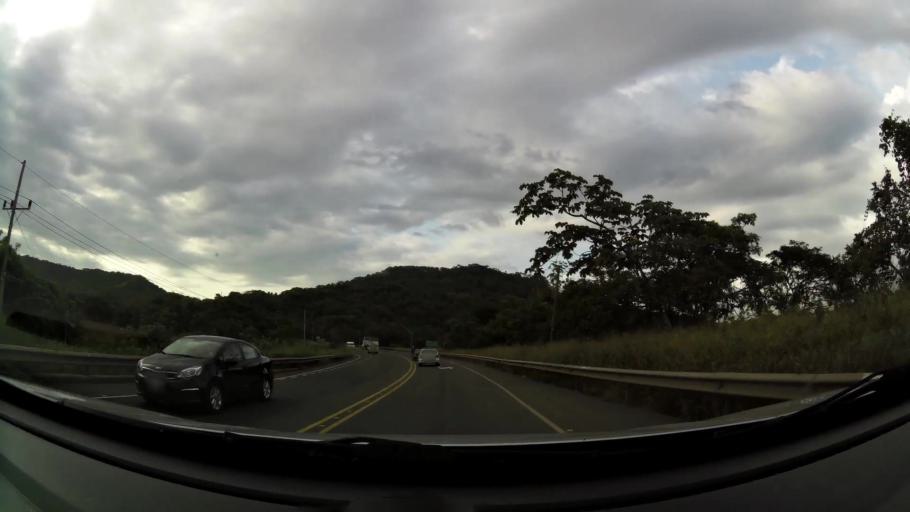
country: CR
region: Puntarenas
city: Esparza
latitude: 9.9128
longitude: -84.6722
